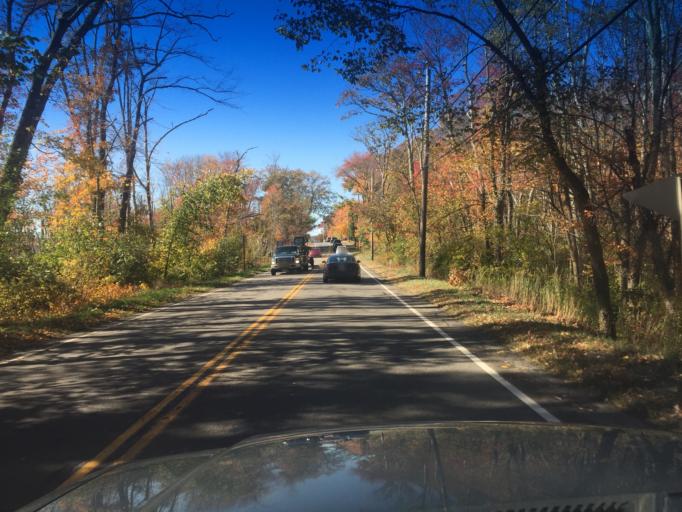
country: US
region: Massachusetts
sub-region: Worcester County
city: Milford
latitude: 42.1466
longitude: -71.4765
